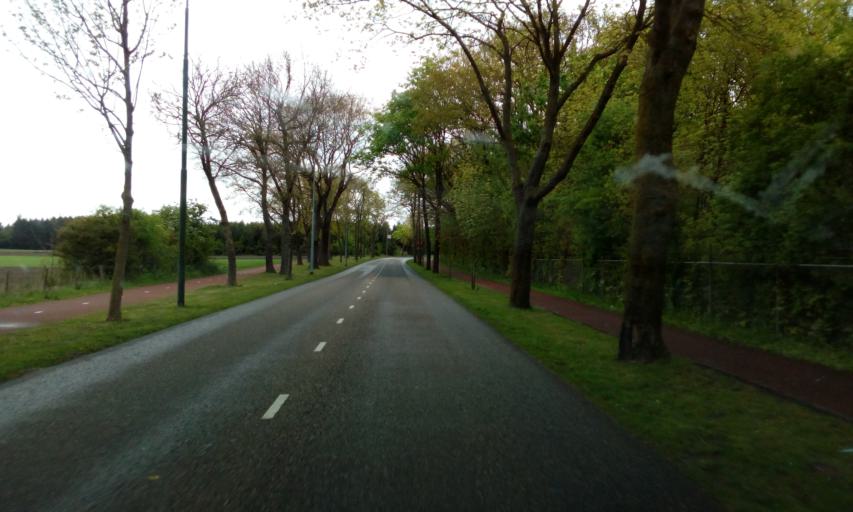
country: NL
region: North Holland
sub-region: Gemeente Huizen
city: Huizen
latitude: 52.2862
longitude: 5.2393
